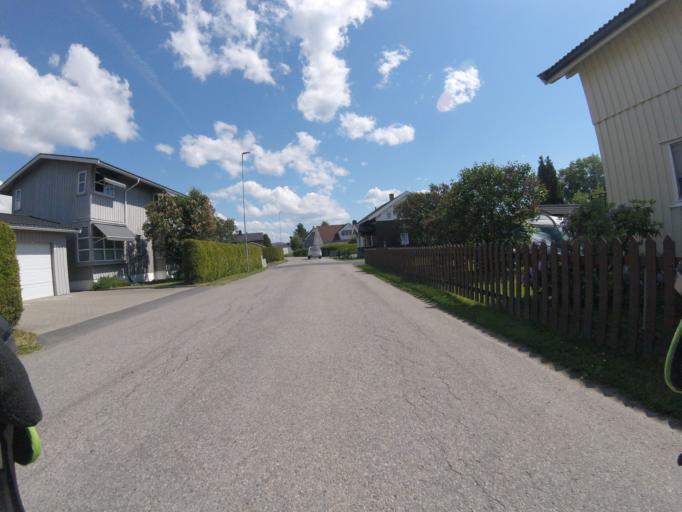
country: NO
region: Akershus
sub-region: Skedsmo
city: Lillestrom
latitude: 59.9516
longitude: 11.0613
